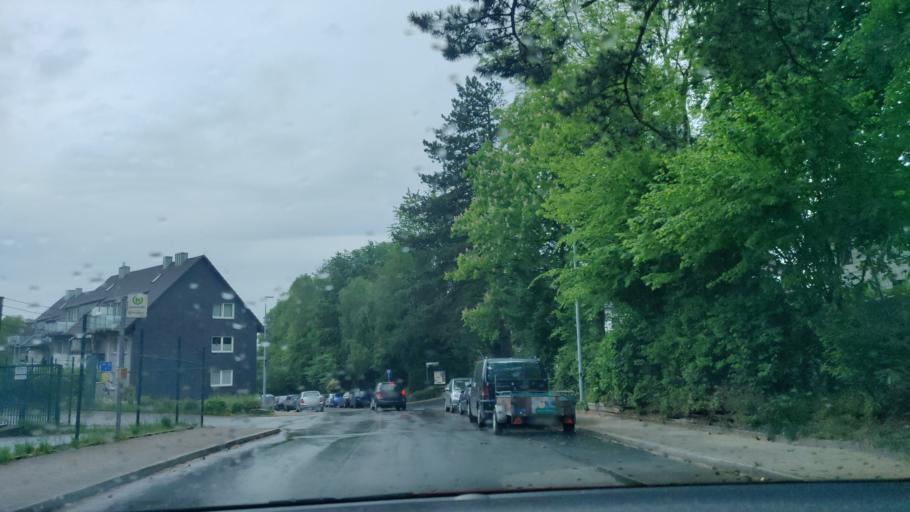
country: DE
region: North Rhine-Westphalia
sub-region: Regierungsbezirk Dusseldorf
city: Heiligenhaus
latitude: 51.3326
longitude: 6.9534
